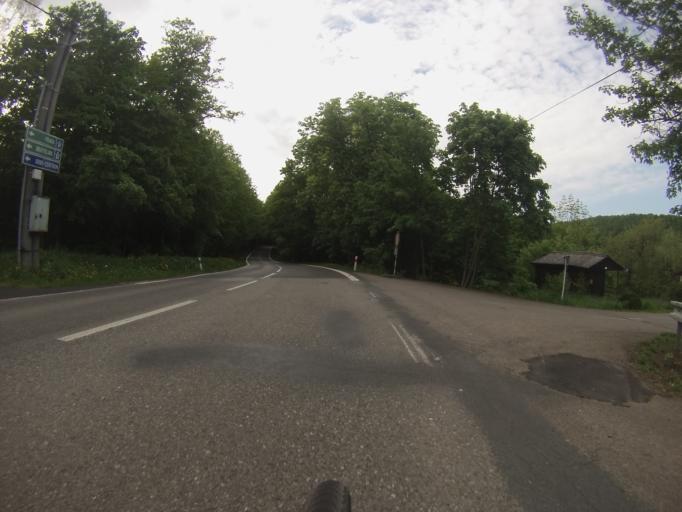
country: CZ
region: South Moravian
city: Veverska Bityska
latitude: 49.2558
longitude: 16.4755
